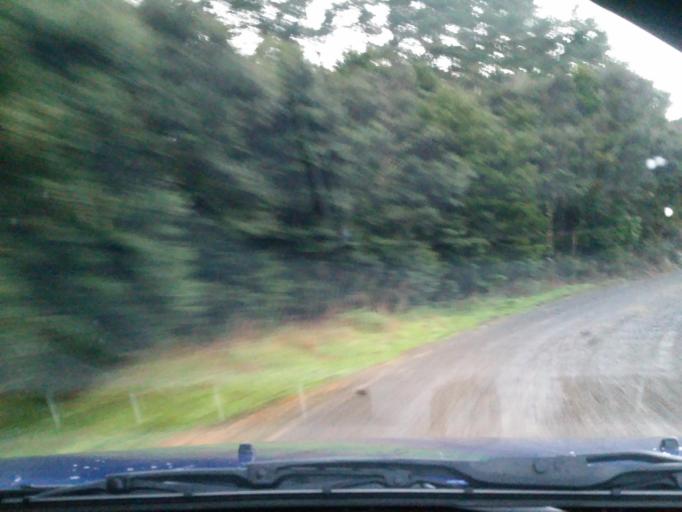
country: NZ
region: Northland
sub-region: Whangarei
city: Maungatapere
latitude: -35.8051
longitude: 174.0456
